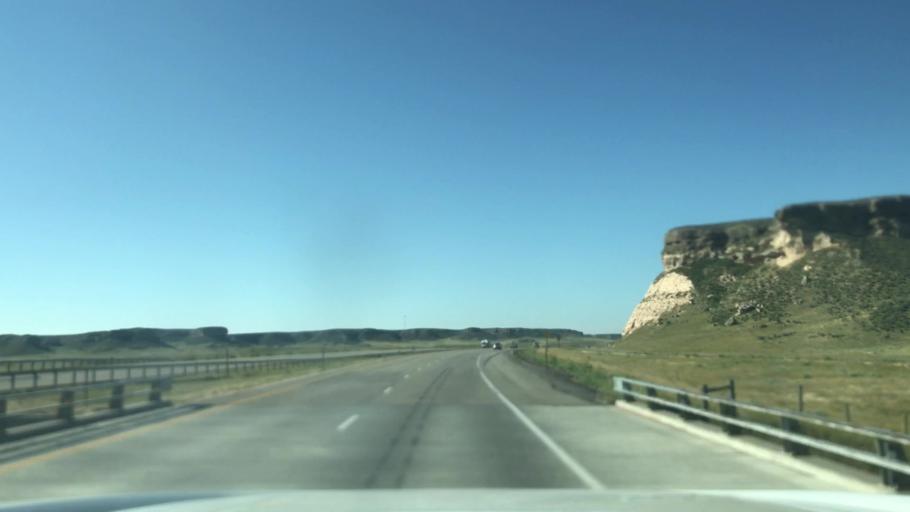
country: US
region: Wyoming
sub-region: Platte County
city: Wheatland
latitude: 41.7843
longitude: -104.7918
